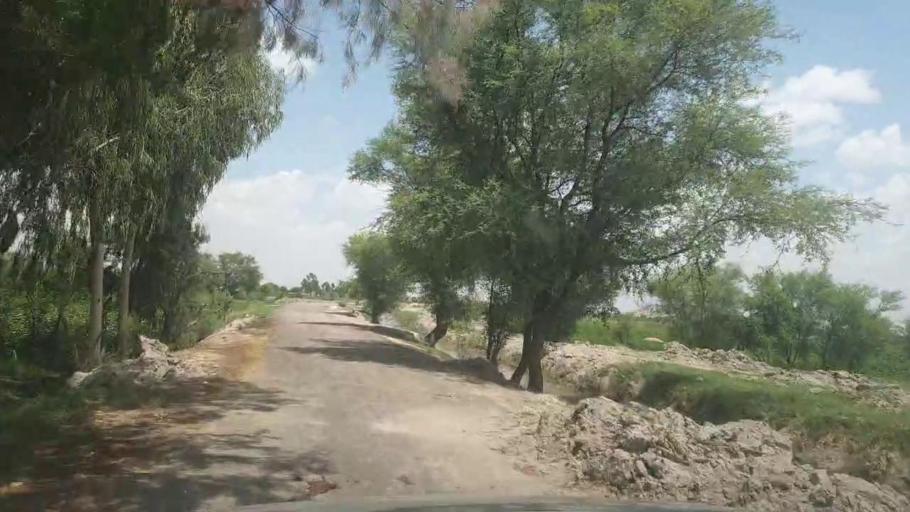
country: PK
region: Sindh
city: Kot Diji
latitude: 27.2357
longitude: 69.0307
